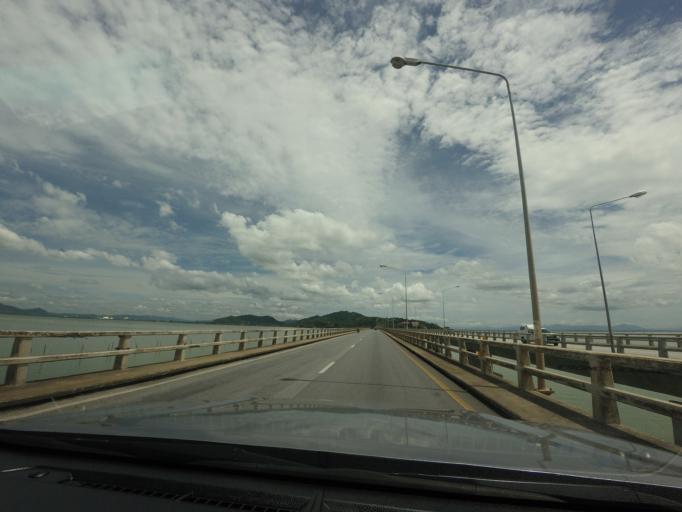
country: TH
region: Songkhla
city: Ban Mai
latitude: 7.1926
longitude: 100.5489
